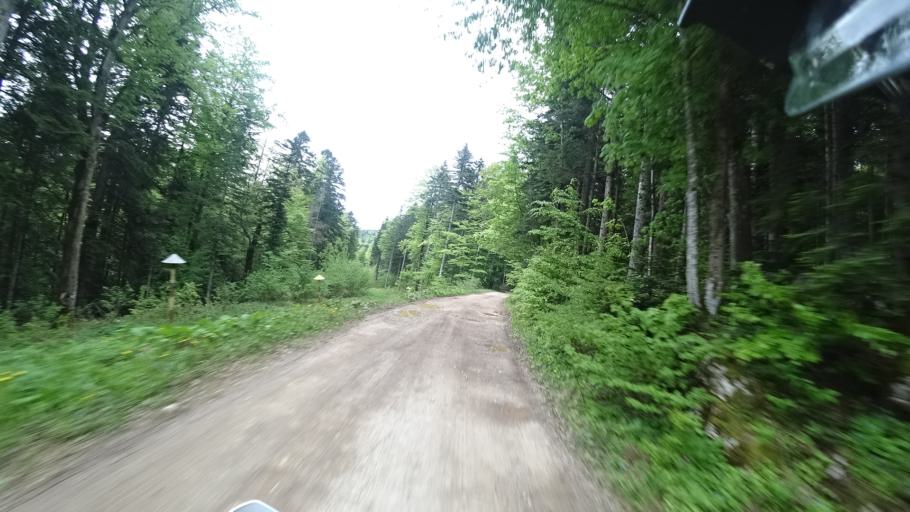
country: HR
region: Karlovacka
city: Plaski
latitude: 44.9619
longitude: 15.4073
